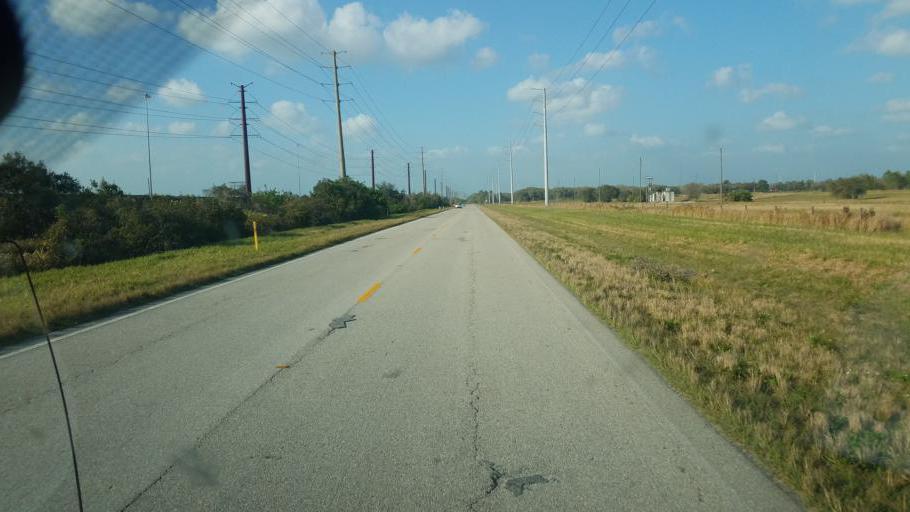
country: US
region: Florida
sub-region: Hardee County
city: Wauchula
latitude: 27.5756
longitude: -81.9360
